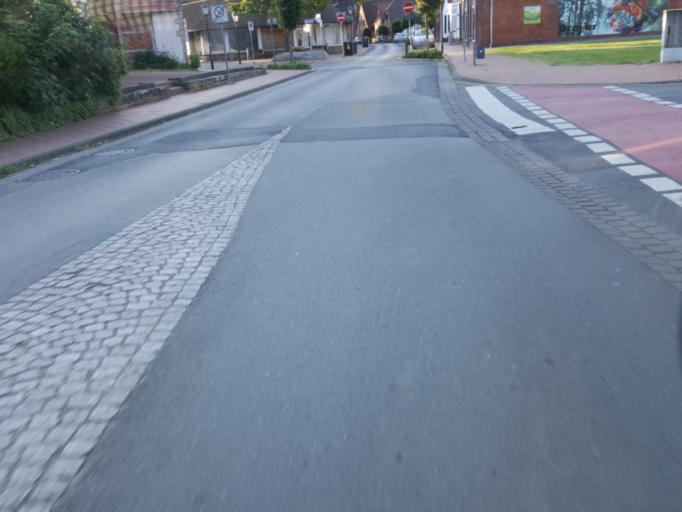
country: DE
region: Lower Saxony
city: Stolzenau
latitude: 52.5115
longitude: 9.0702
